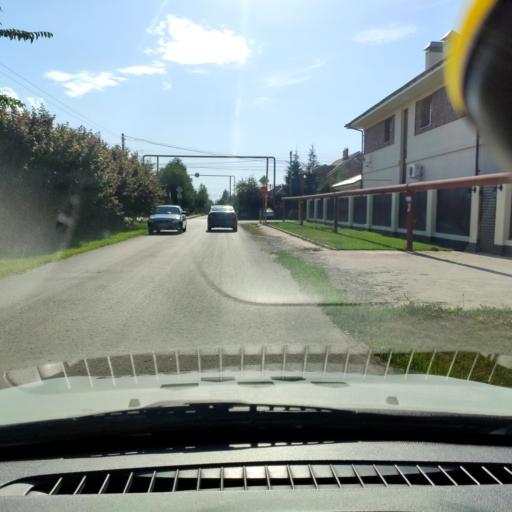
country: RU
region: Samara
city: Podstepki
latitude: 53.5178
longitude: 49.1820
